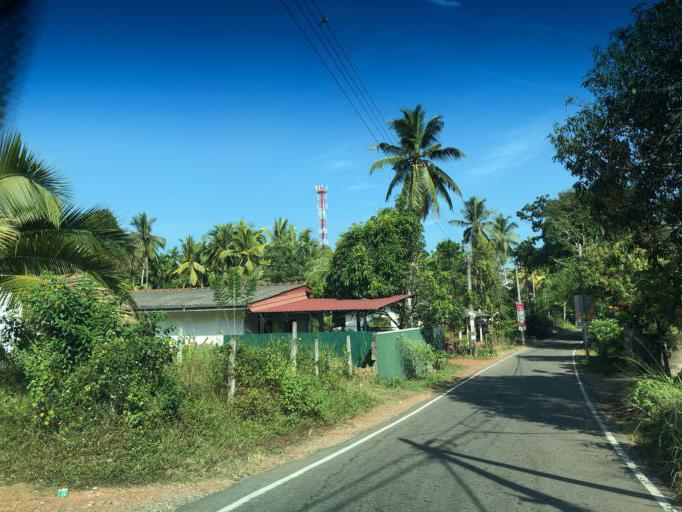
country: LK
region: Western
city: Homagama
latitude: 6.8038
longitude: 79.9788
